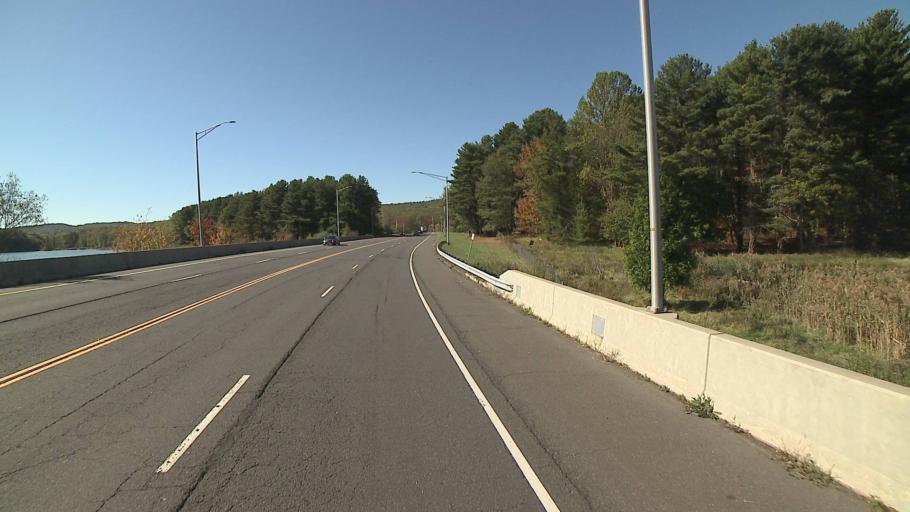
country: US
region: Connecticut
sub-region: Middlesex County
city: Durham
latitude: 41.5389
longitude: -72.7218
